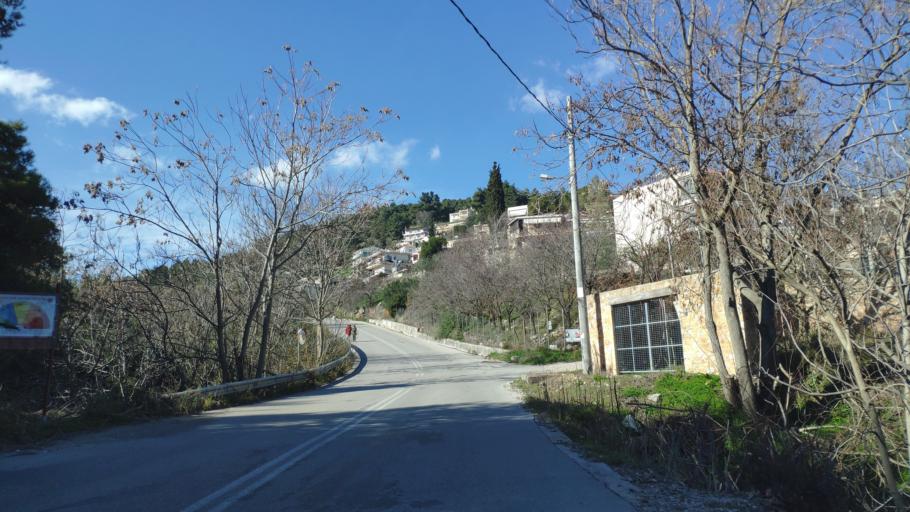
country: GR
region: Attica
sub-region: Nomarchia Anatolikis Attikis
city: Afidnes
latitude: 38.2033
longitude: 23.8361
